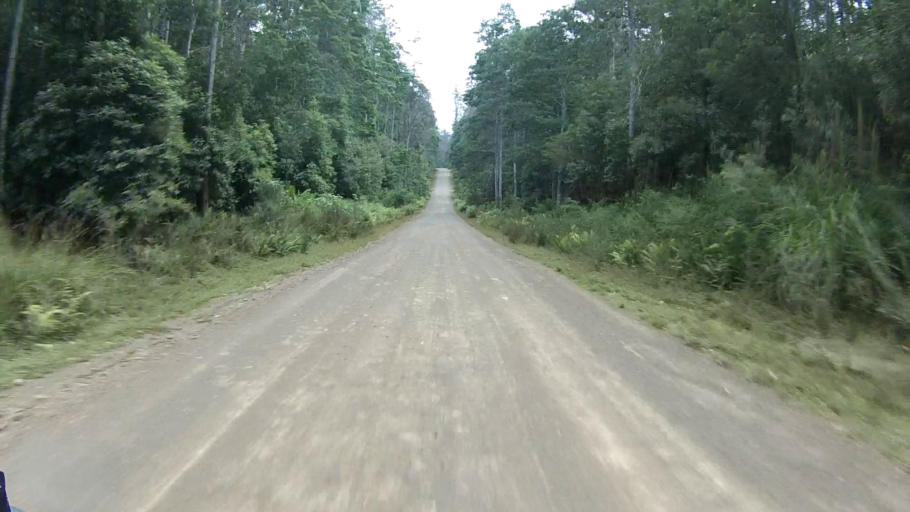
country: AU
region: Tasmania
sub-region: Sorell
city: Sorell
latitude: -42.7168
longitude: 147.8413
